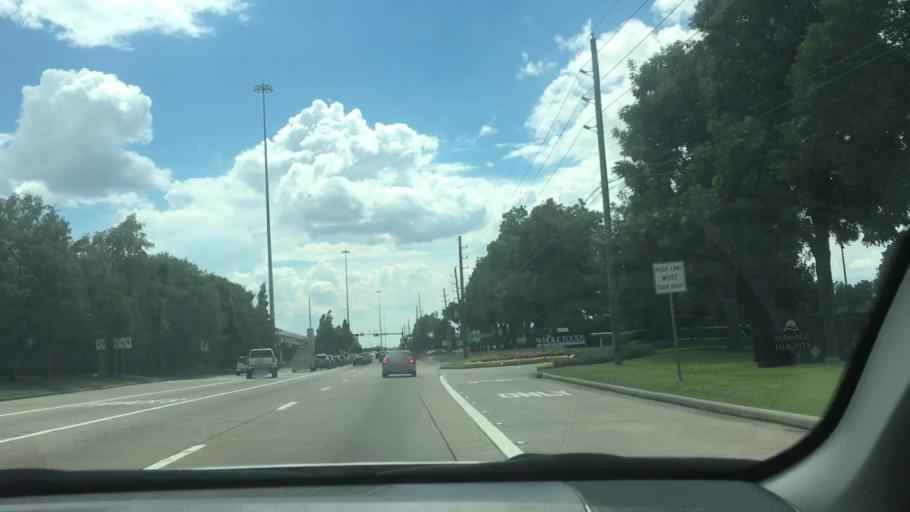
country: US
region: Texas
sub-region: Fort Bend County
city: Sugar Land
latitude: 29.6000
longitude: -95.6216
